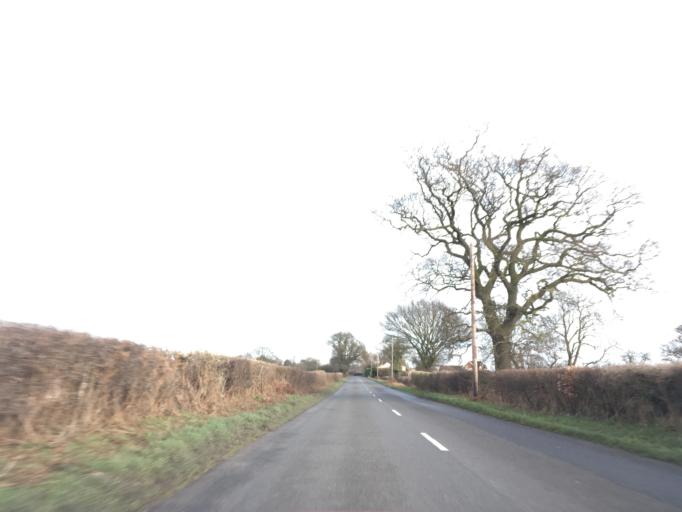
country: GB
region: England
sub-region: Nottinghamshire
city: South Collingham
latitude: 53.1816
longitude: -0.7531
